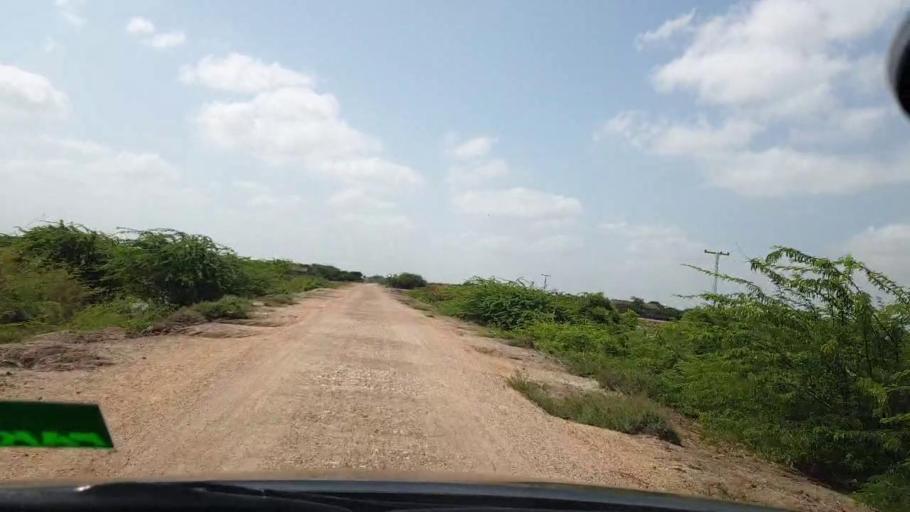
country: PK
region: Sindh
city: Kadhan
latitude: 24.5821
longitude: 69.1525
